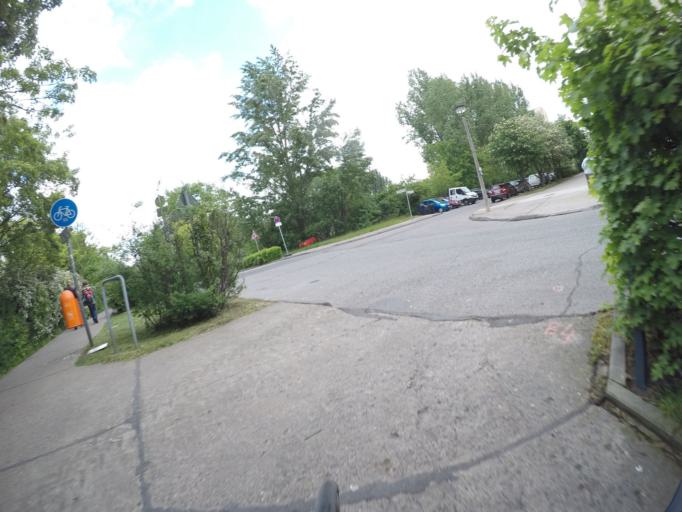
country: DE
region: Berlin
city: Marzahn
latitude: 52.5582
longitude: 13.5686
